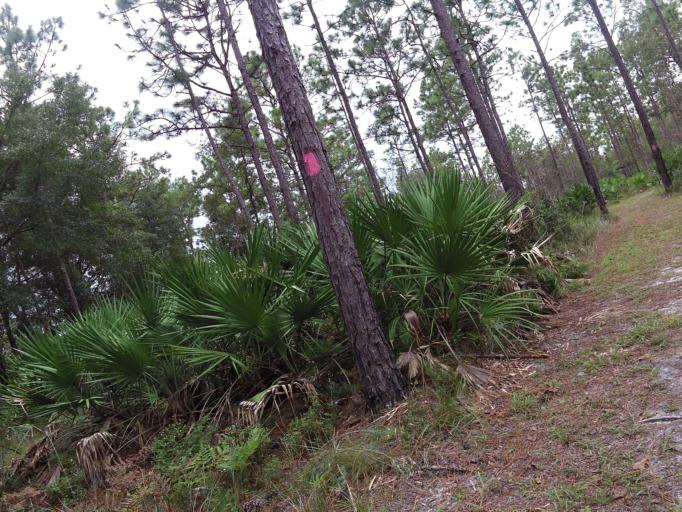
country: US
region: Florida
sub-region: Clay County
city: Middleburg
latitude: 30.1288
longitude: -81.9634
